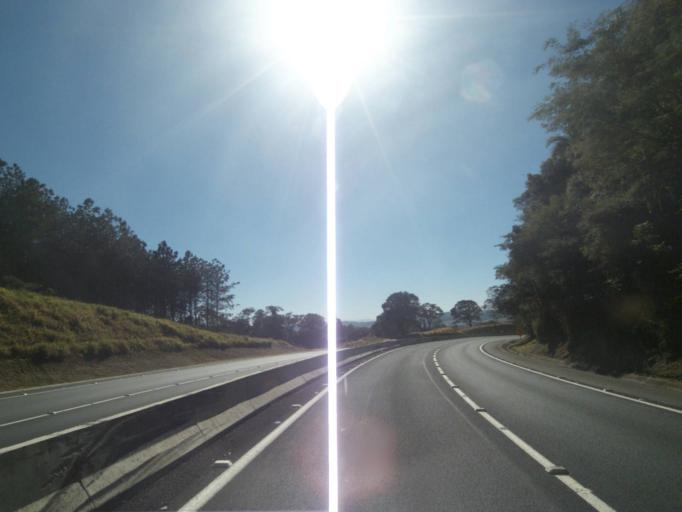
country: BR
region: Parana
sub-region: Tibagi
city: Tibagi
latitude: -24.8086
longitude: -50.4909
